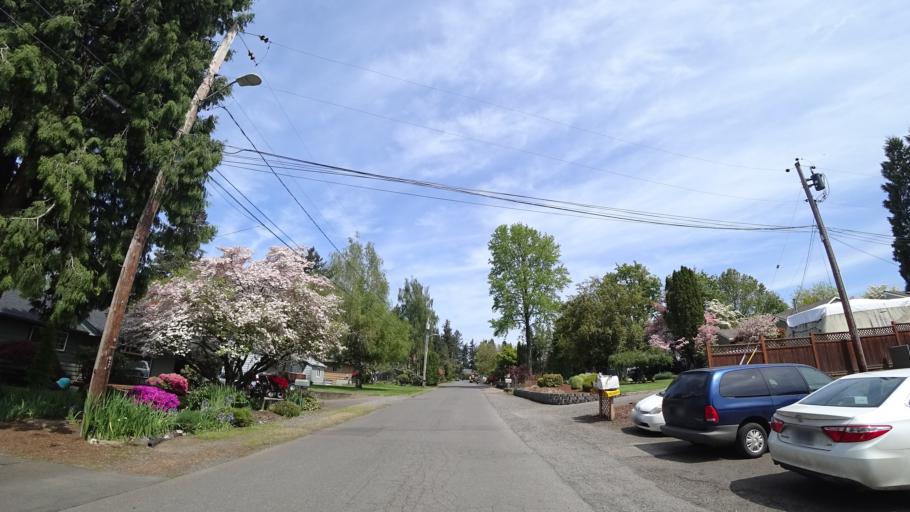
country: US
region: Oregon
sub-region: Clackamas County
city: Milwaukie
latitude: 45.4461
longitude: -122.6093
